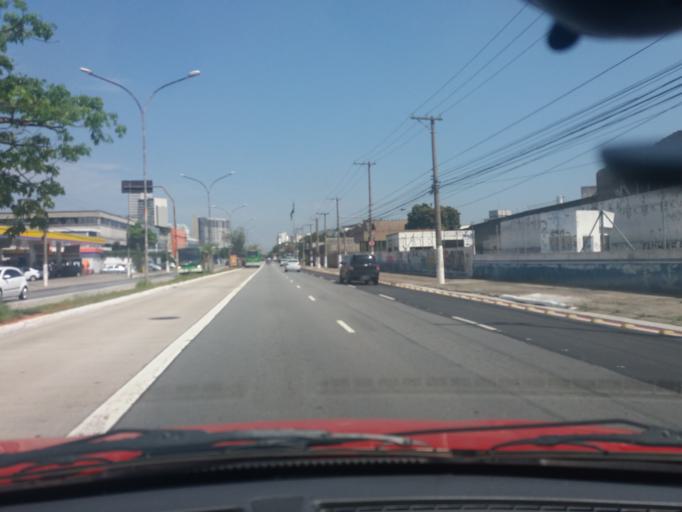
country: BR
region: Sao Paulo
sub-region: Sao Paulo
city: Sao Paulo
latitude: -23.5206
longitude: -46.6700
